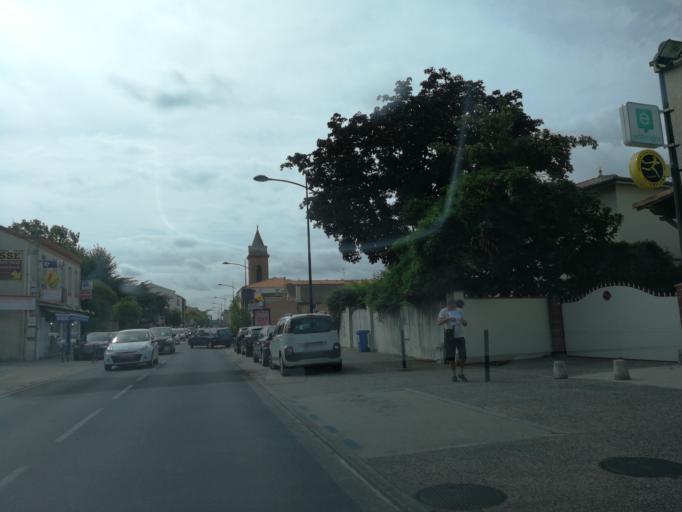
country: FR
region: Midi-Pyrenees
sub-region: Departement de la Haute-Garonne
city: Aucamville
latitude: 43.6676
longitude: 1.4293
